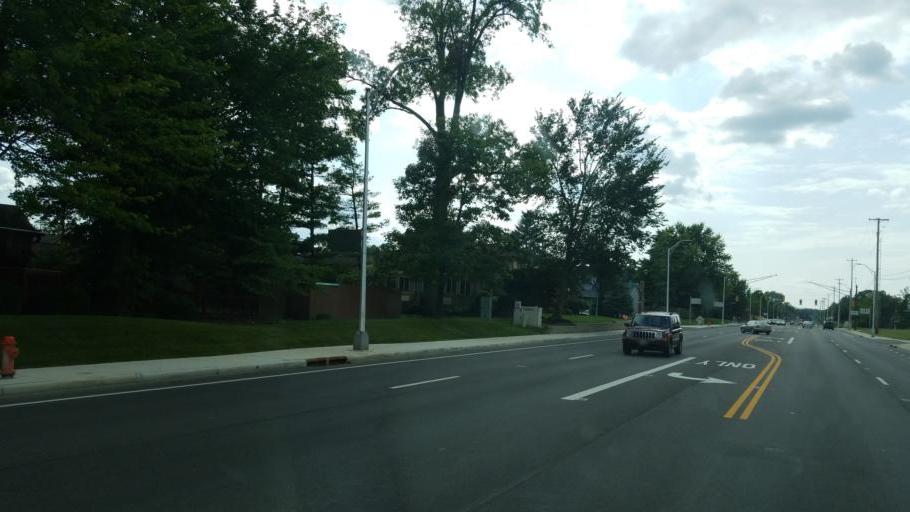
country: US
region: Ohio
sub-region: Delaware County
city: Powell
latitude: 40.1175
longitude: -83.0740
